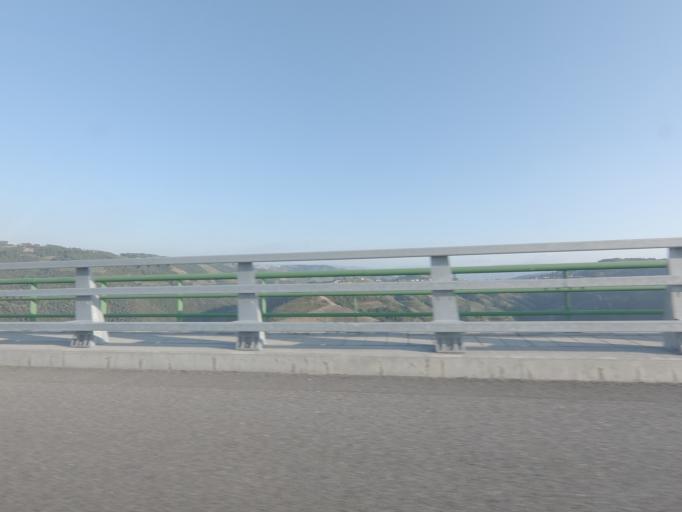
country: PT
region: Vila Real
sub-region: Vila Real
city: Vila Real
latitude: 41.2785
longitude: -7.7581
